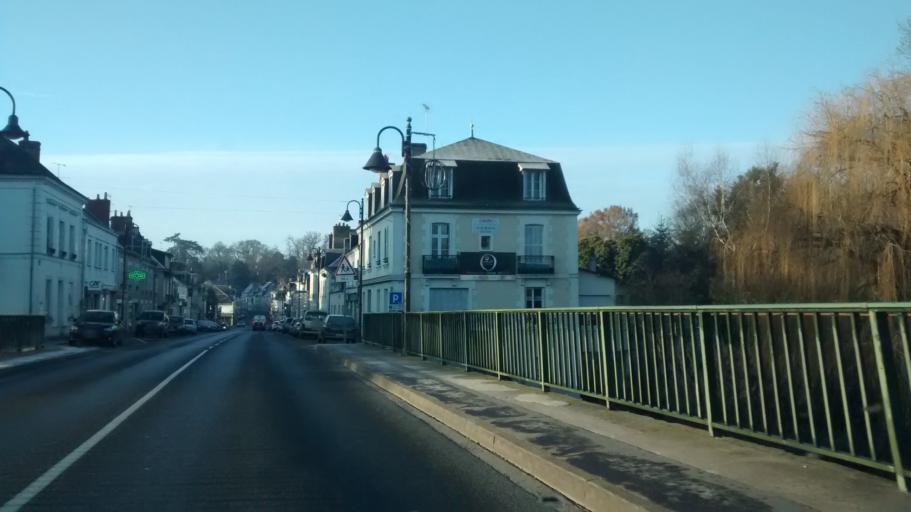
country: FR
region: Centre
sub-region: Departement d'Indre-et-Loire
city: Montbazon
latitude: 47.2887
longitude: 0.7164
